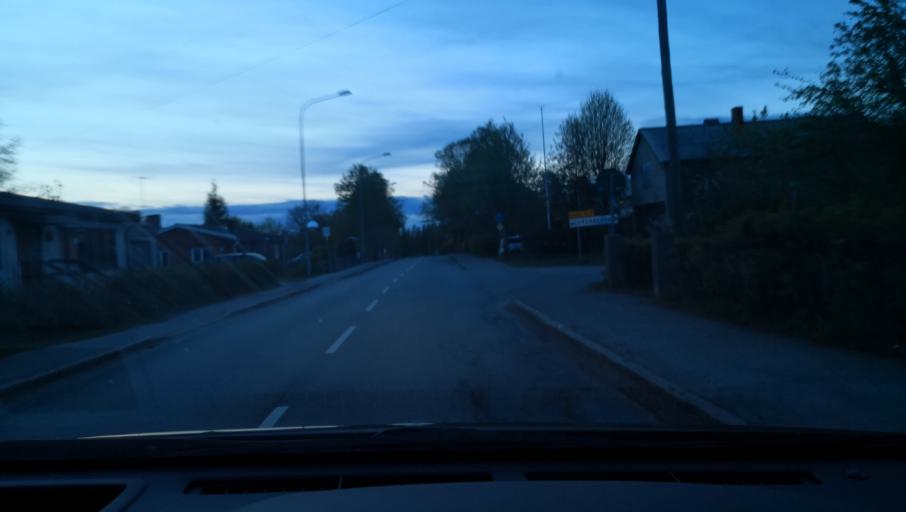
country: SE
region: OErebro
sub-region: Lekebergs Kommun
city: Fjugesta
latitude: 59.0256
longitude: 14.8672
